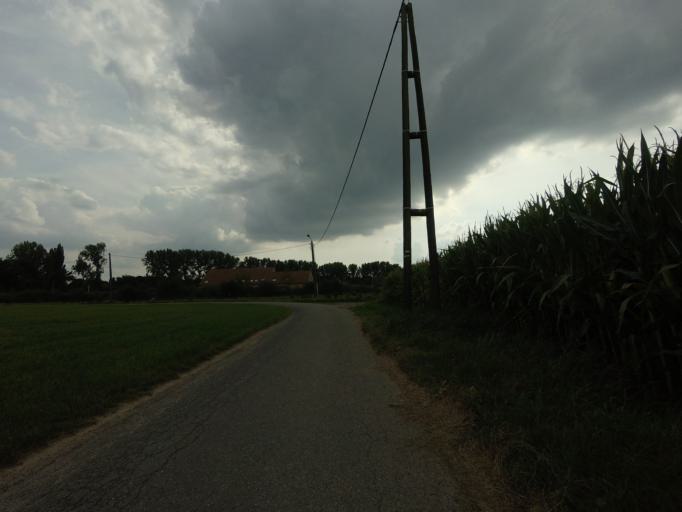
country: BE
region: Flanders
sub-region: Provincie Antwerpen
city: Edegem
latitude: 51.1481
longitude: 4.4162
